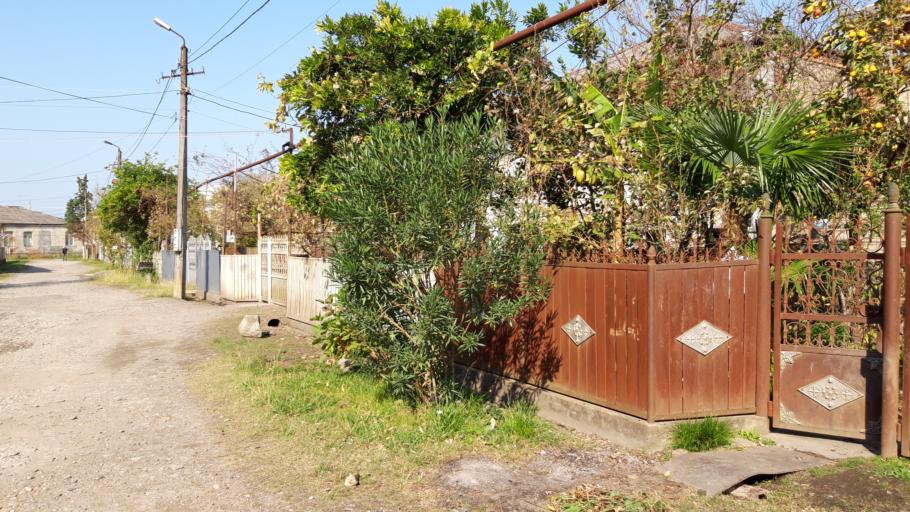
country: GE
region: Imereti
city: Samtredia
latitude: 42.1613
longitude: 42.3336
